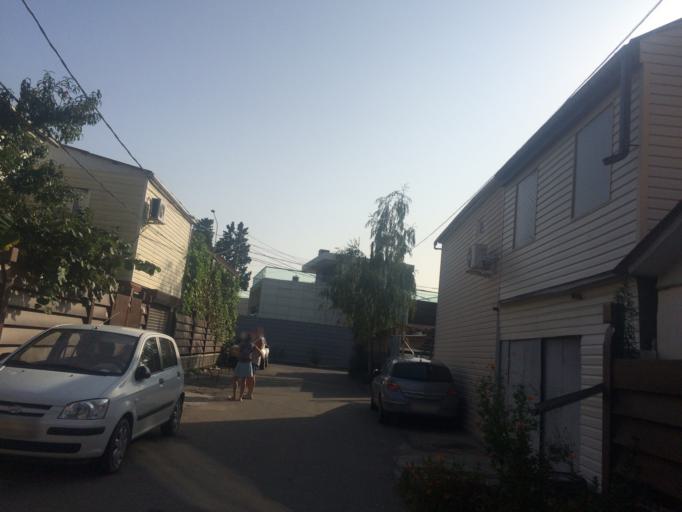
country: RU
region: Krasnodarskiy
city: Adler
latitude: 43.3923
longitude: 39.9792
